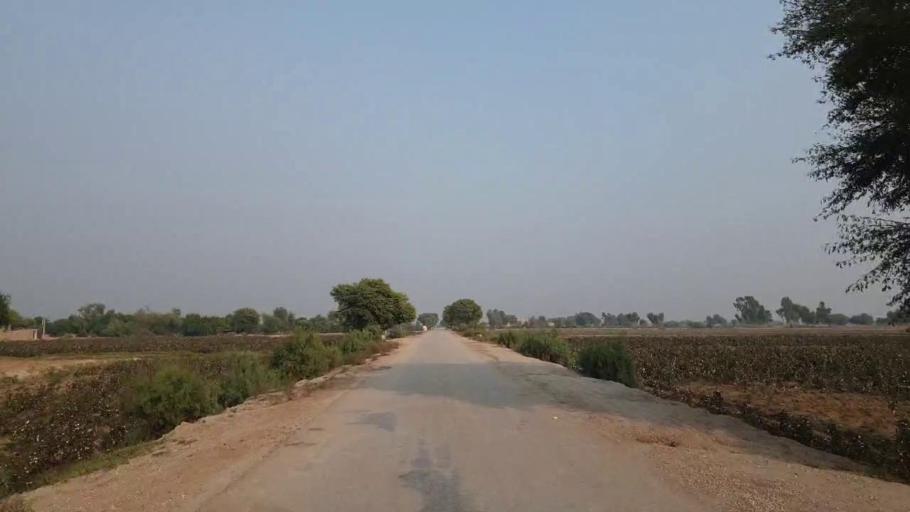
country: PK
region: Sindh
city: Bhan
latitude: 26.4954
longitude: 67.7262
